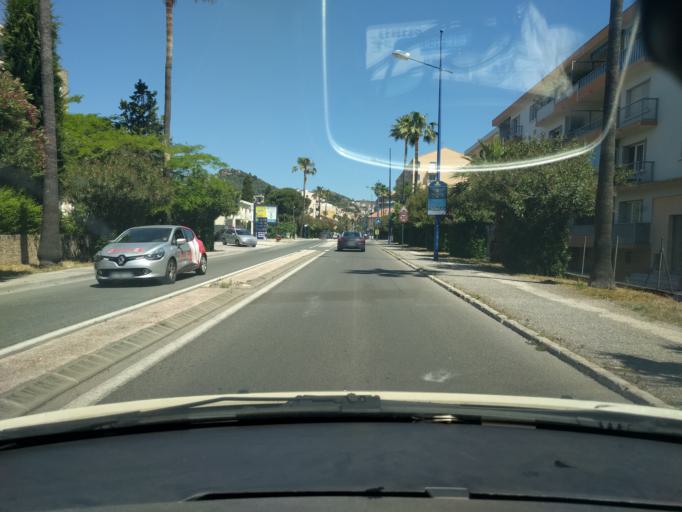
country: FR
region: Provence-Alpes-Cote d'Azur
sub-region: Departement du Var
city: Hyeres
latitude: 43.1104
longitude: 6.1288
